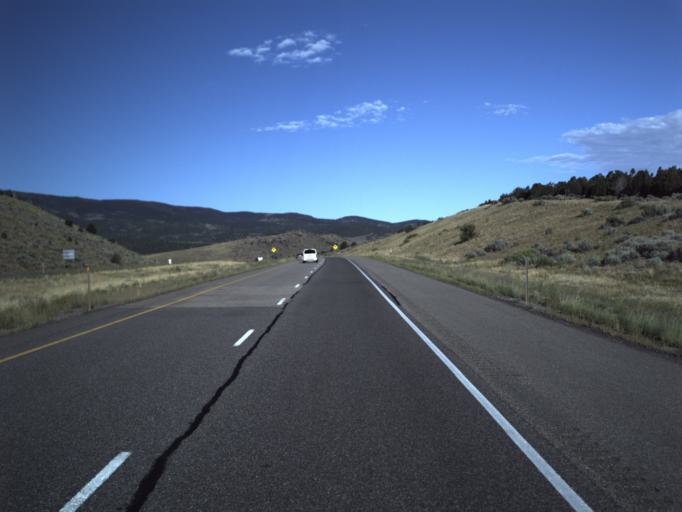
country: US
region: Utah
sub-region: Sevier County
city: Monroe
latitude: 38.5531
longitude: -112.4102
